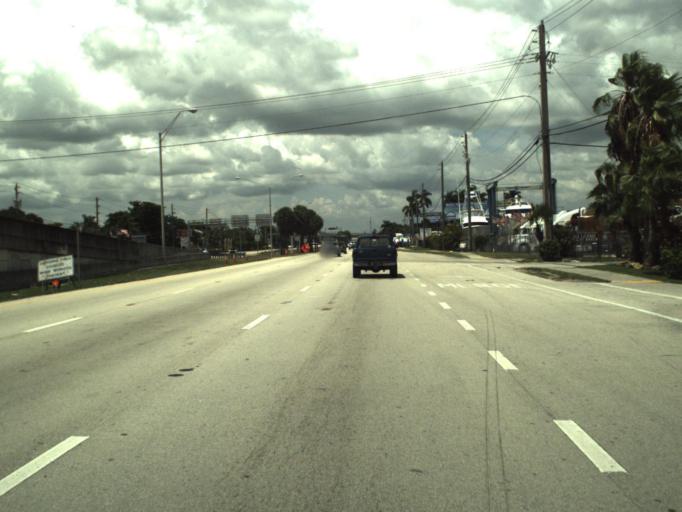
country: US
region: Florida
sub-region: Broward County
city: Melrose Park
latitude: 26.0879
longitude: -80.1720
